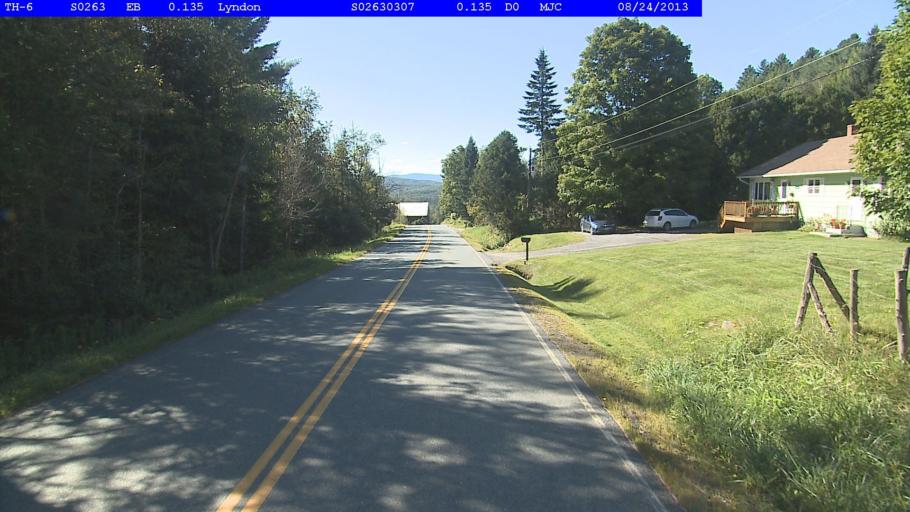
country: US
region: Vermont
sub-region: Caledonia County
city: Lyndon
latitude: 44.4941
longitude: -71.9719
